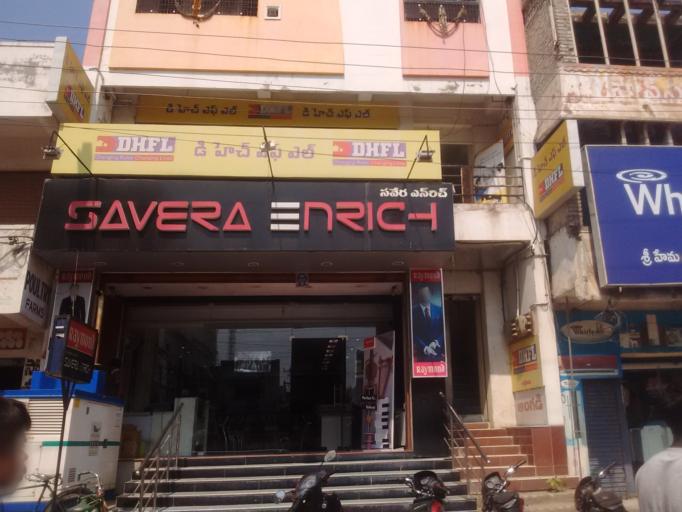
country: IN
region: Telangana
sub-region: Mahbubnagar
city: Alampur
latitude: 15.8295
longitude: 78.0417
